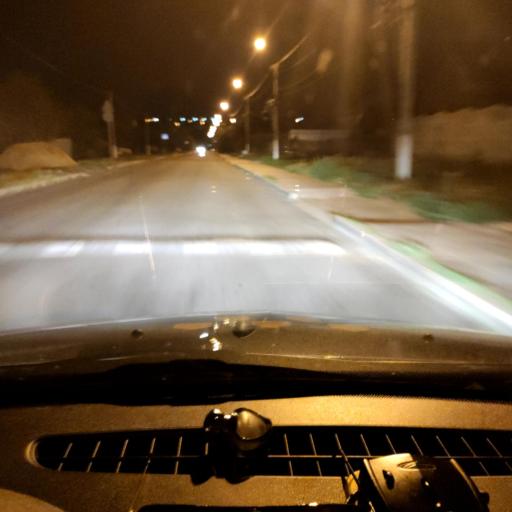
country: RU
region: Belgorod
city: Mayskiy
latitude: 50.5185
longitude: 36.4583
